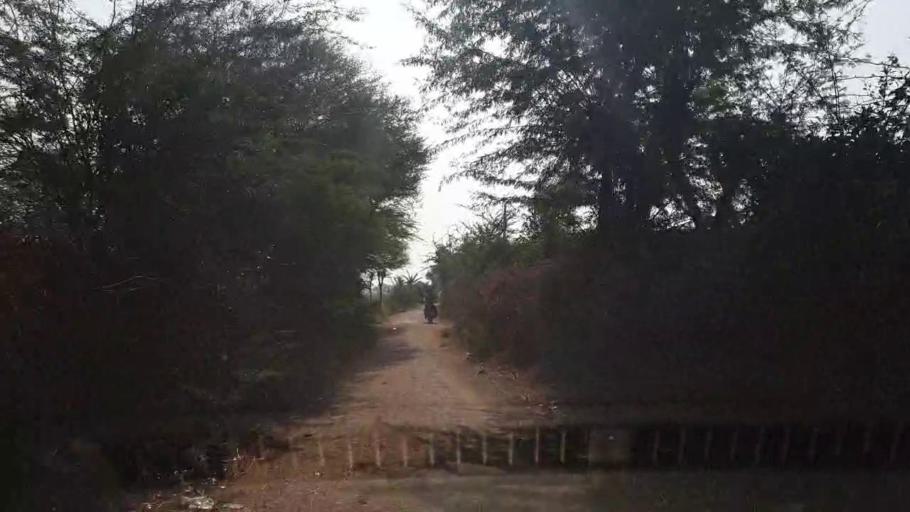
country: PK
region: Sindh
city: Matli
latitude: 24.9759
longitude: 68.6146
